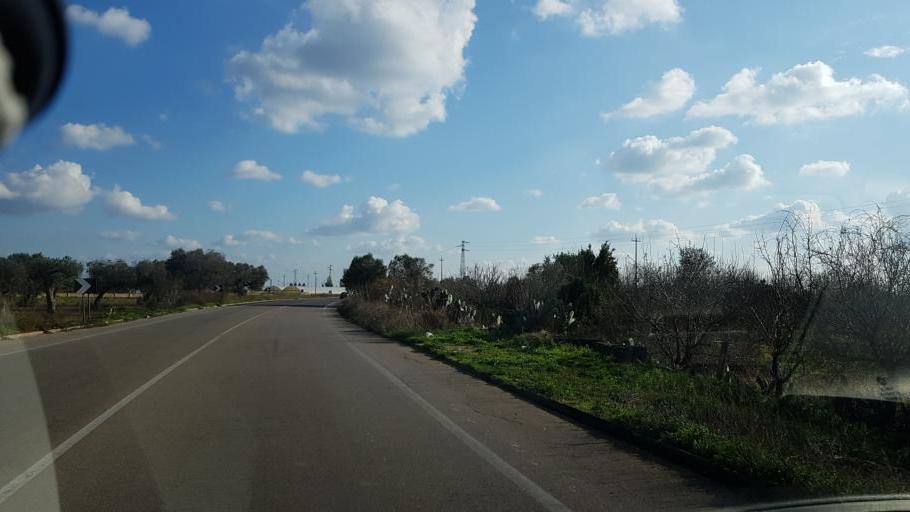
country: IT
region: Apulia
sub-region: Provincia di Lecce
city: Veglie
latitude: 40.3481
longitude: 17.9725
